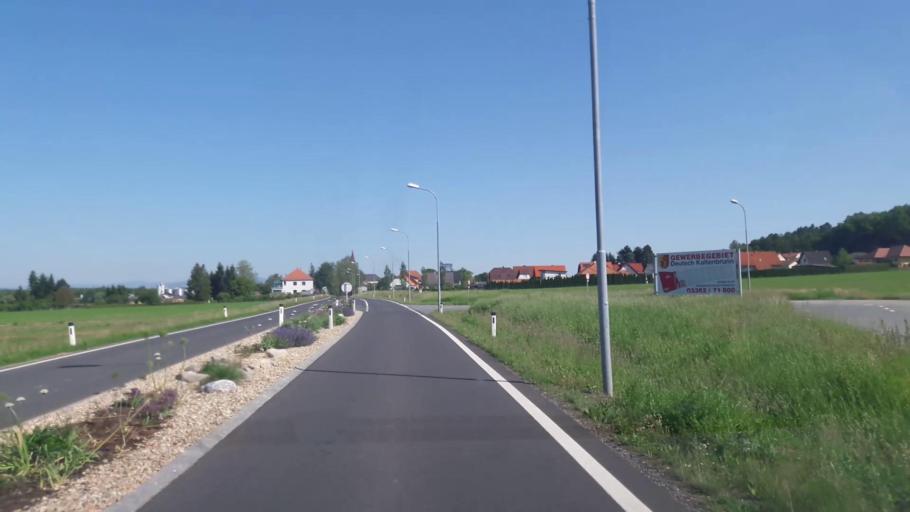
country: AT
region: Burgenland
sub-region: Politischer Bezirk Jennersdorf
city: Deutsch Kaltenbrunn
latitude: 47.0790
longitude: 16.1107
